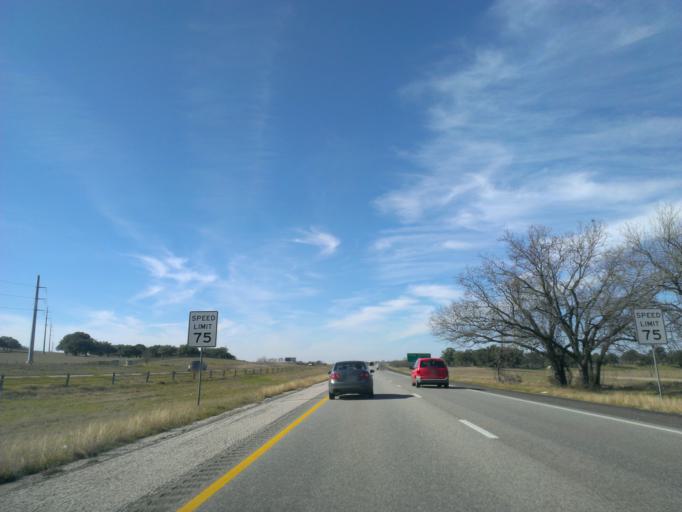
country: US
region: Texas
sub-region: Bell County
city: Nolanville
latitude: 31.0626
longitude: -97.5684
